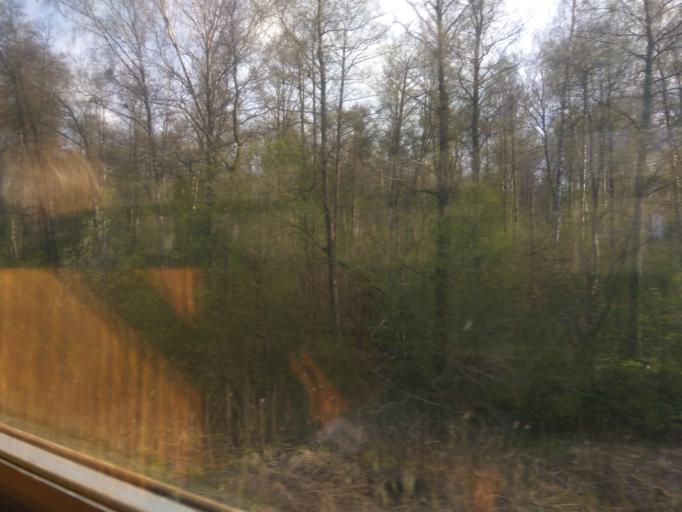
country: LV
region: Babite
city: Pinki
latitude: 56.9670
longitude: 23.9065
